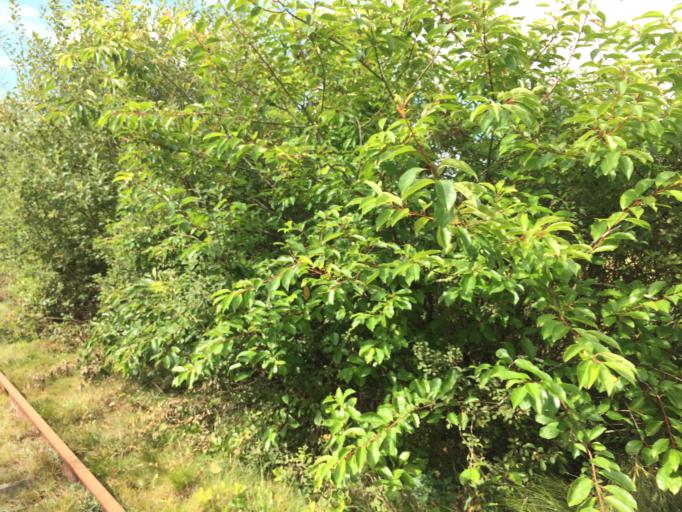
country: DK
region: South Denmark
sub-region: Varde Kommune
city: Oksbol
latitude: 55.7841
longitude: 8.2592
